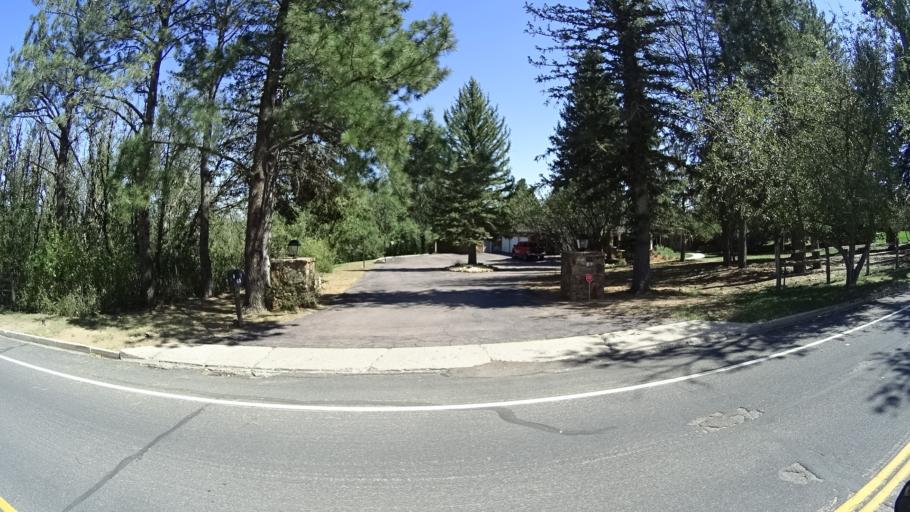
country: US
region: Colorado
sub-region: El Paso County
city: Colorado Springs
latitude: 38.7838
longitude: -104.8436
